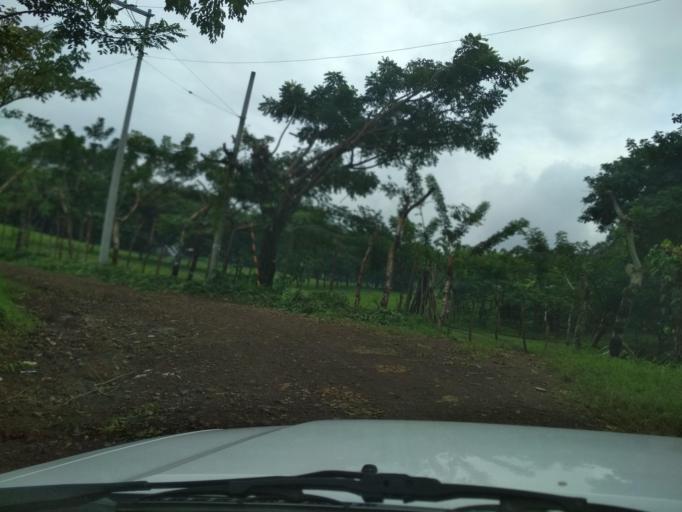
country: MX
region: Veracruz
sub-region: San Andres Tuxtla
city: Matacapan
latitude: 18.4347
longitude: -95.1505
